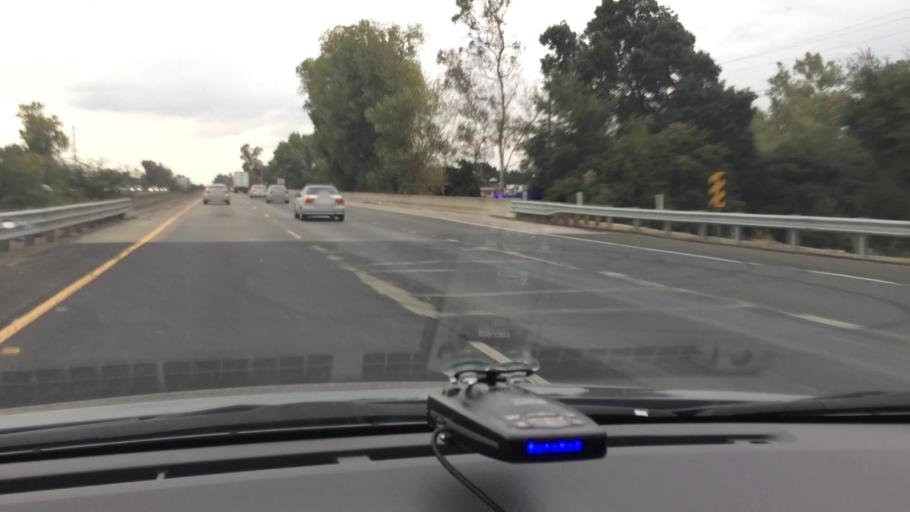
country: US
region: California
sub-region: San Joaquin County
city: Lodi
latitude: 38.1475
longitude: -121.2612
